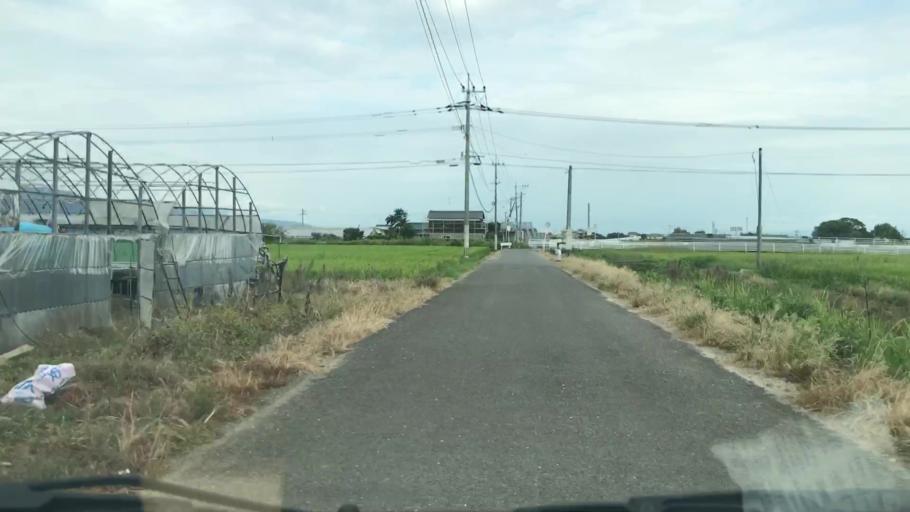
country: JP
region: Saga Prefecture
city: Saga-shi
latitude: 33.2911
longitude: 130.2343
